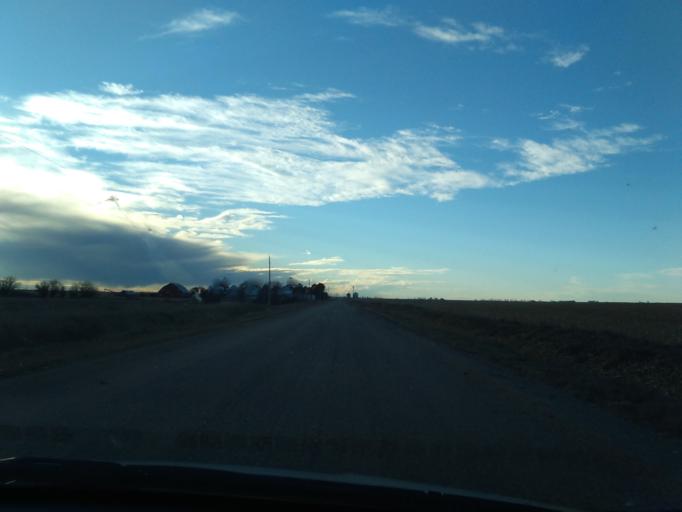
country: US
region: Nebraska
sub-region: Phelps County
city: Holdrege
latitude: 40.4091
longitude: -99.2816
